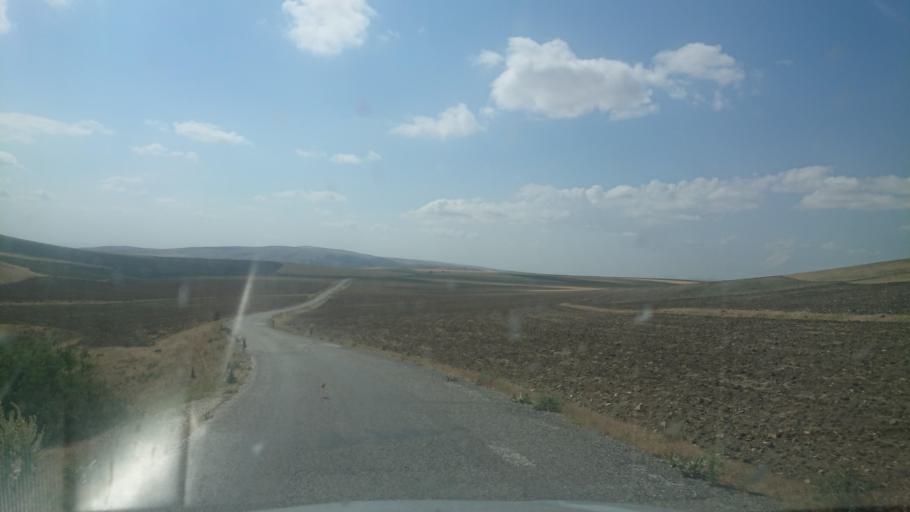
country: TR
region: Aksaray
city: Sariyahsi
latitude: 38.9997
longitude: 33.9756
